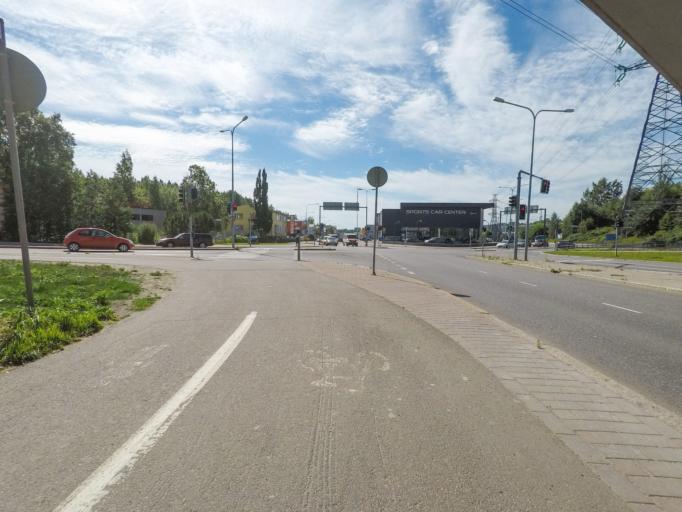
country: FI
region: Uusimaa
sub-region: Helsinki
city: Vantaa
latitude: 60.2076
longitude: 25.0545
